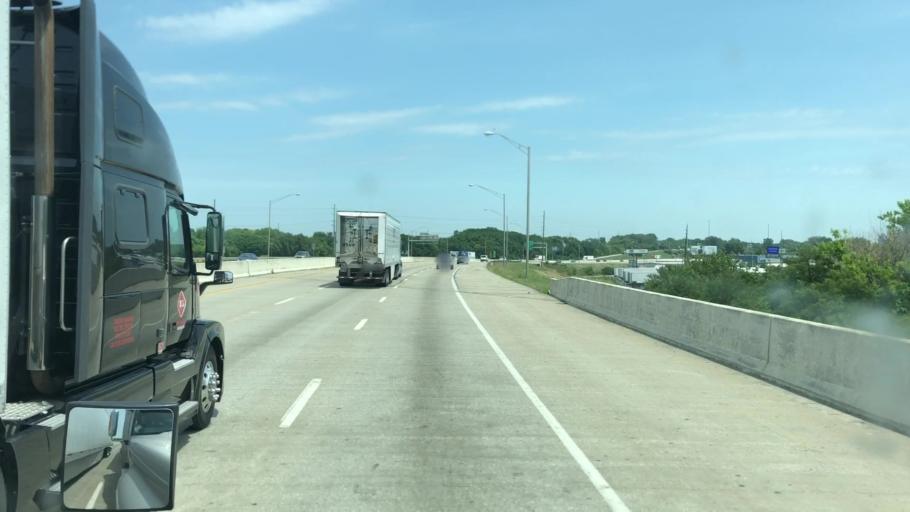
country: US
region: Indiana
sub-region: Marion County
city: Speedway
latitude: 39.7477
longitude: -86.2351
